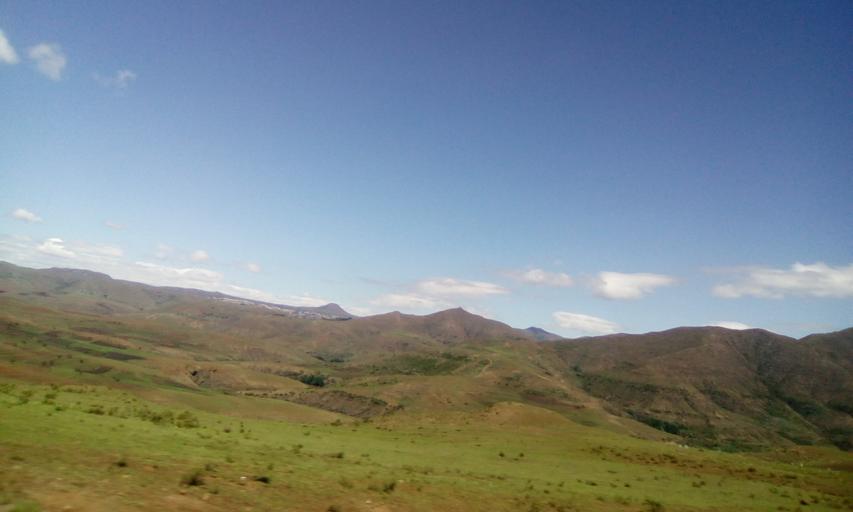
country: LS
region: Maseru
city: Nako
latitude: -29.6293
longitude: 27.7655
